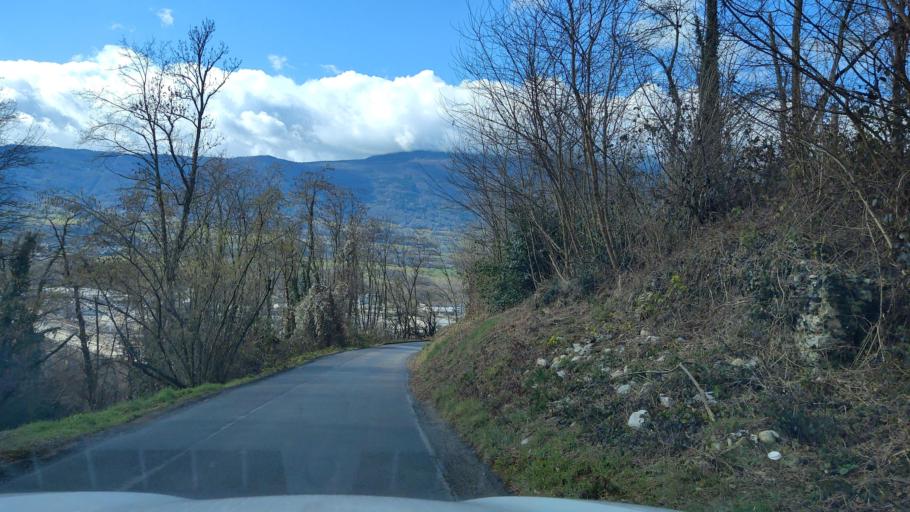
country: FR
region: Rhone-Alpes
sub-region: Departement de la Savoie
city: Sonnaz
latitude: 45.6109
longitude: 5.8983
